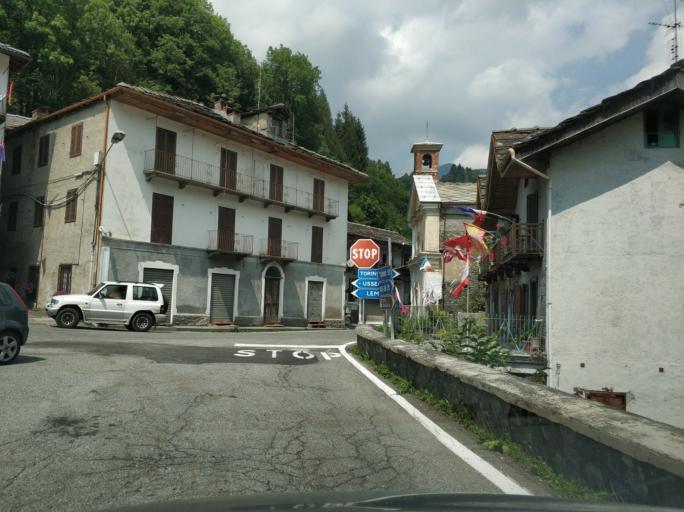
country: IT
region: Piedmont
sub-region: Provincia di Torino
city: Viu
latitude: 45.2320
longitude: 7.3673
